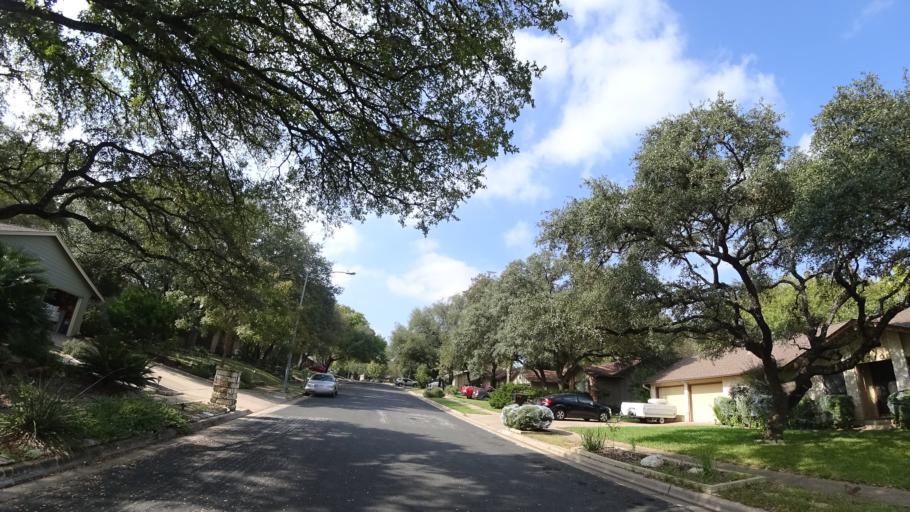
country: US
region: Texas
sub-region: Travis County
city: Shady Hollow
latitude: 30.2062
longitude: -97.8174
